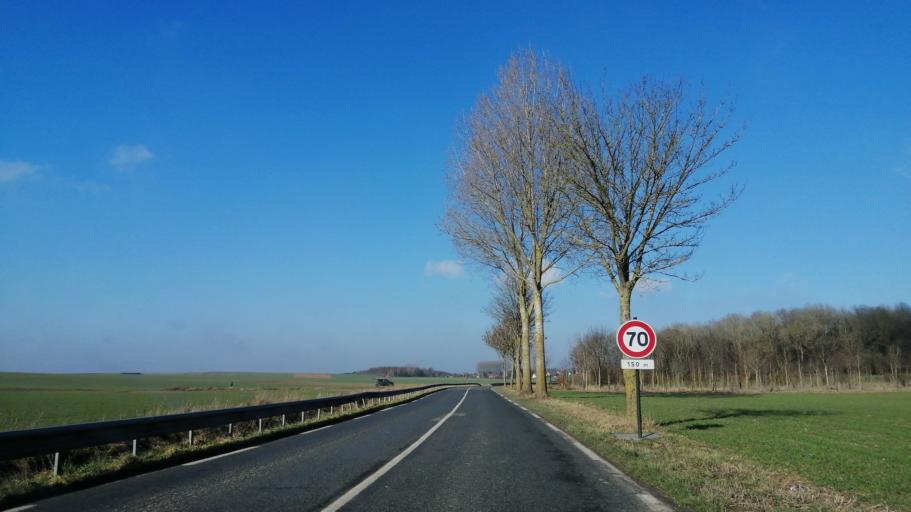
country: FR
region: Nord-Pas-de-Calais
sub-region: Departement du Pas-de-Calais
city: Mont-Saint-Eloi
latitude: 50.3648
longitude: 2.6526
